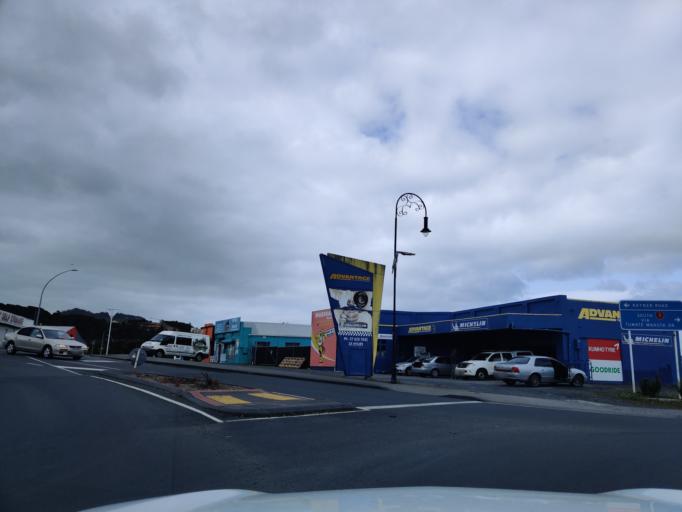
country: NZ
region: Waikato
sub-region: Waikato District
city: Ngaruawahia
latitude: -37.5614
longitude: 175.1585
